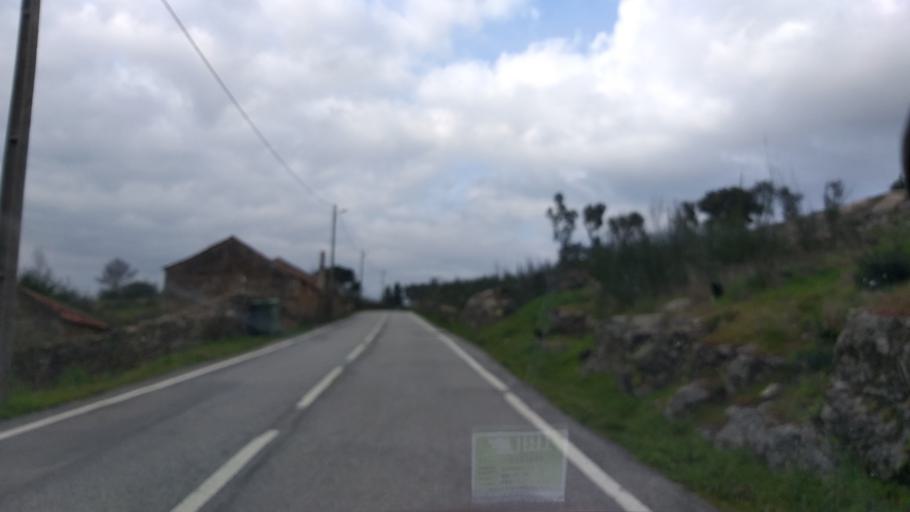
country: PT
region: Guarda
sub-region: Seia
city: Seia
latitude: 40.4851
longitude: -7.6327
